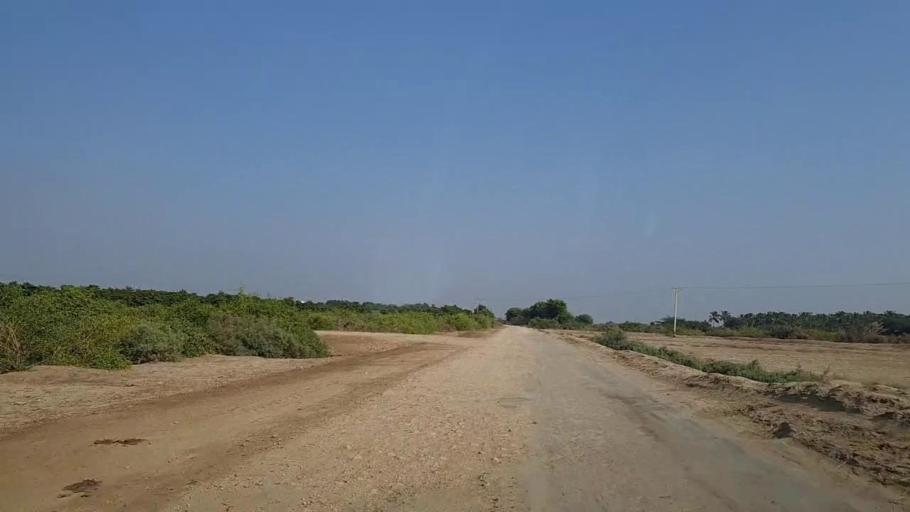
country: PK
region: Sindh
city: Mirpur Sakro
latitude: 24.6195
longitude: 67.6632
